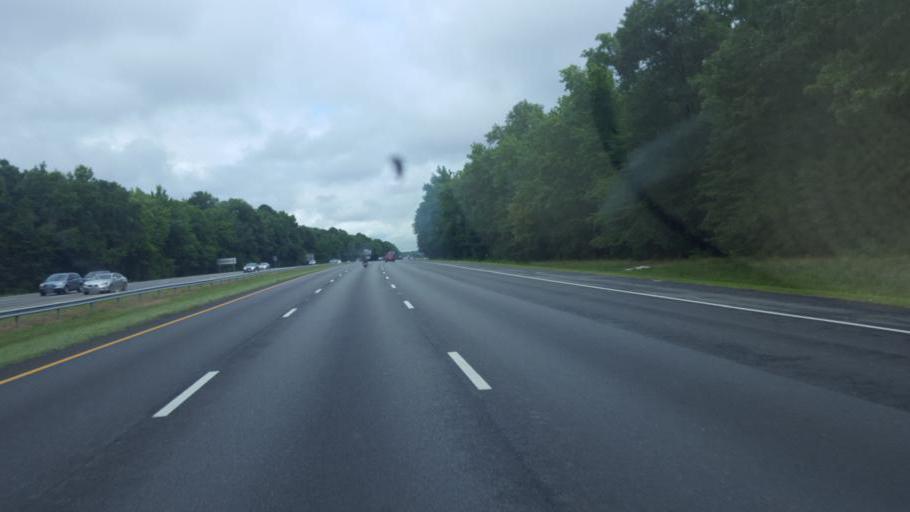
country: US
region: Virginia
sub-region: Henrico County
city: Chamberlayne
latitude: 37.6426
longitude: -77.4524
